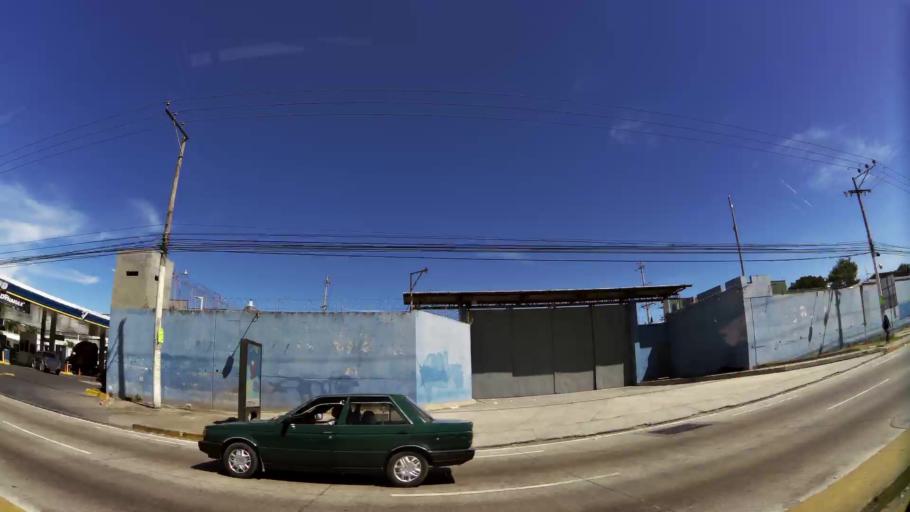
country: SV
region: San Salvador
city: Apopa
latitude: 13.7906
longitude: -89.1753
